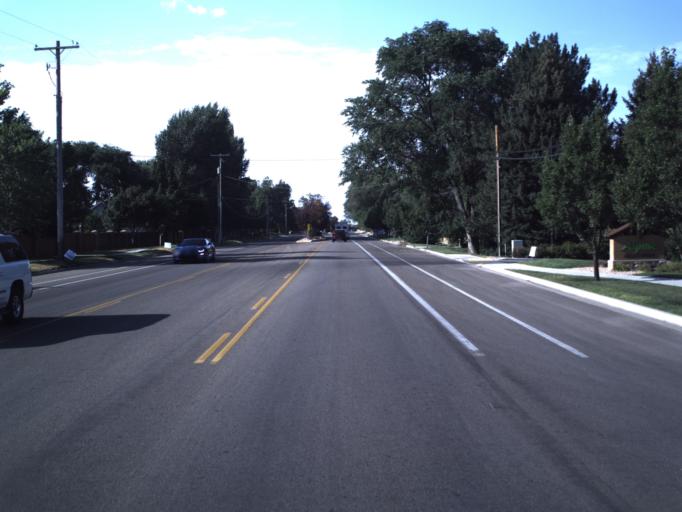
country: US
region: Utah
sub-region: Utah County
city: Alpine
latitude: 40.4290
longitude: -111.7855
